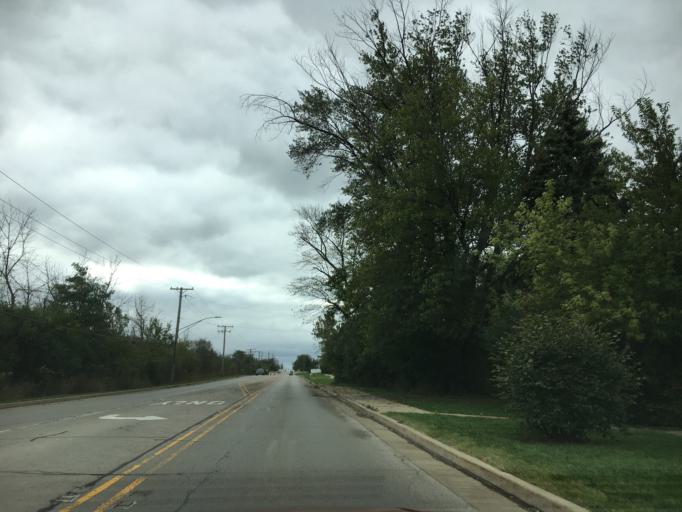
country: US
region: Illinois
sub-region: Cook County
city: Tinley Park
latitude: 41.6119
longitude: -87.7857
